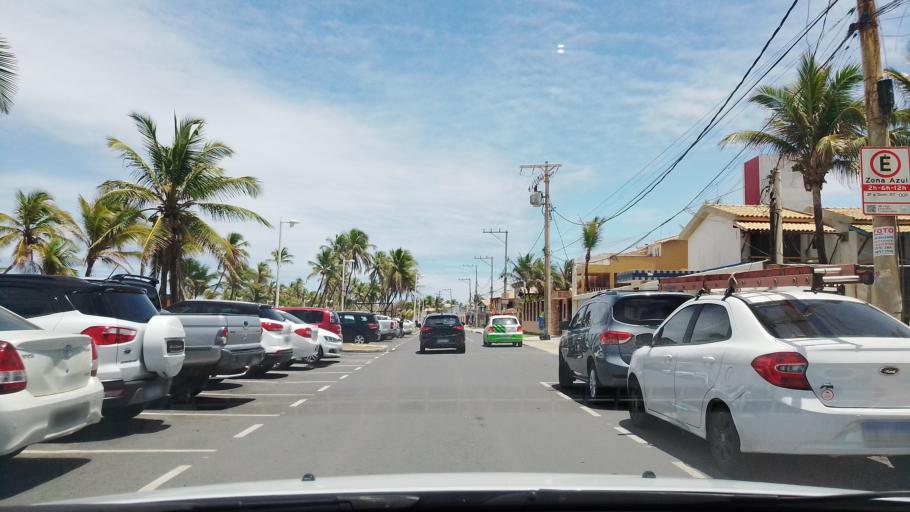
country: BR
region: Bahia
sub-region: Lauro De Freitas
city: Lauro de Freitas
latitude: -12.9392
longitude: -38.3302
